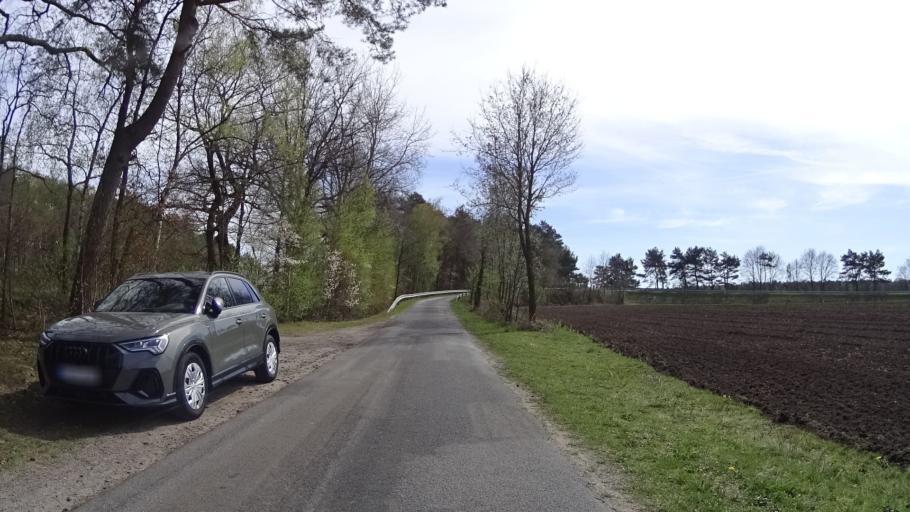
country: DE
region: Lower Saxony
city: Lunne
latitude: 52.3916
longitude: 7.3884
